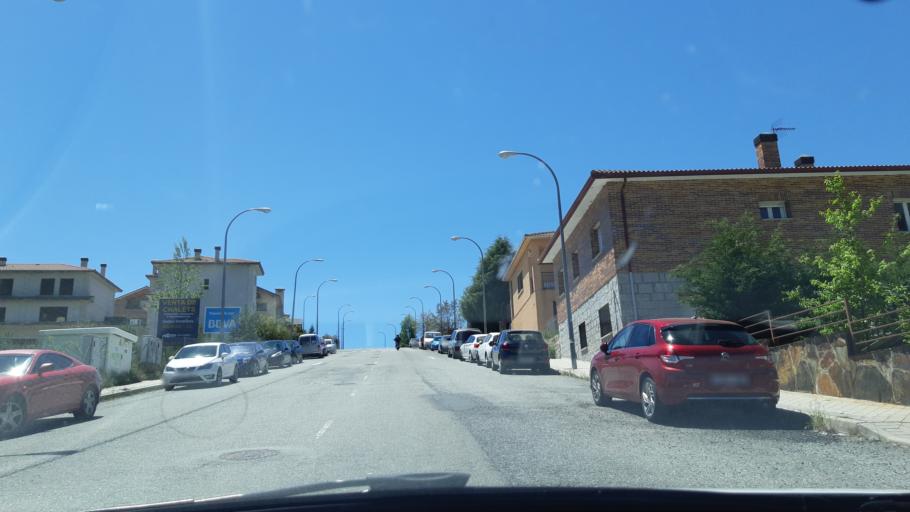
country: ES
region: Castille and Leon
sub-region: Provincia de Avila
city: Peguerinos
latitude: 40.7198
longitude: -4.1929
